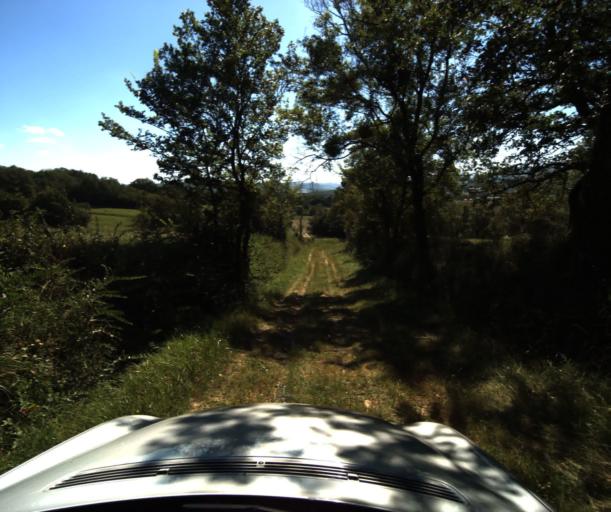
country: FR
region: Midi-Pyrenees
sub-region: Departement de l'Ariege
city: Lavelanet
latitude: 42.9956
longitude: 1.9008
